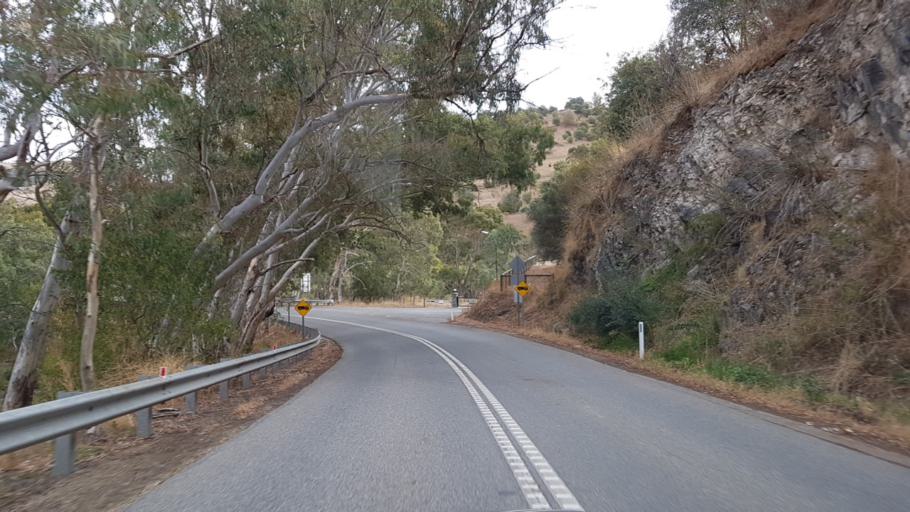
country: AU
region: South Australia
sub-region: Campbelltown
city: Athelstone
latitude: -34.8641
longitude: 138.7591
